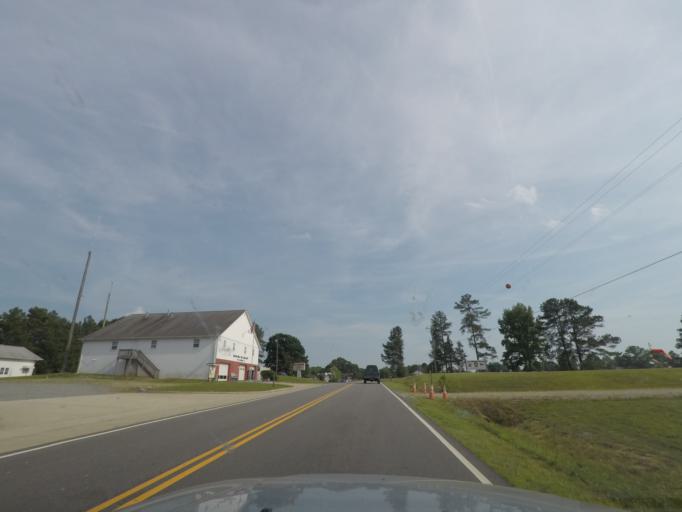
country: US
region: Virginia
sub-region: Mecklenburg County
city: Chase City
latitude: 36.8400
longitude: -78.5950
